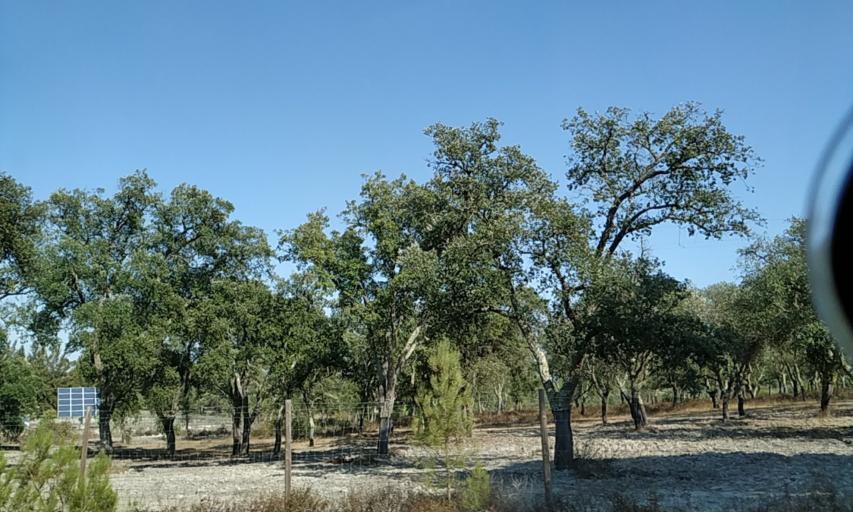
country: PT
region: Santarem
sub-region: Coruche
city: Coruche
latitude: 38.8179
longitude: -8.5712
